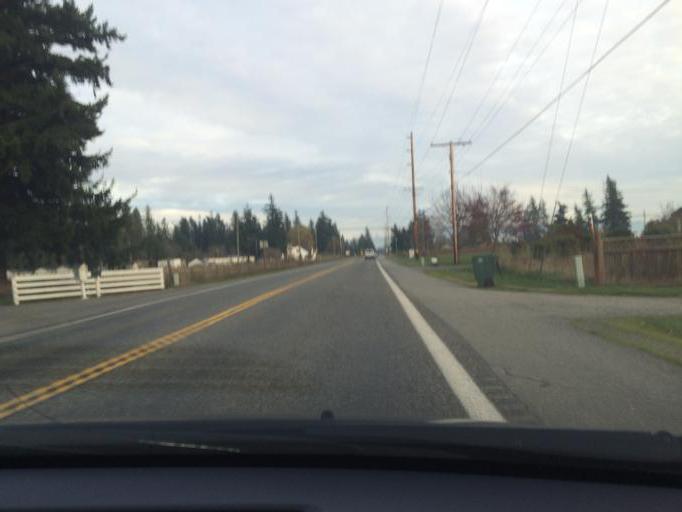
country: US
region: Washington
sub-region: Whatcom County
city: Lynden
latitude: 48.9353
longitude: -122.5315
